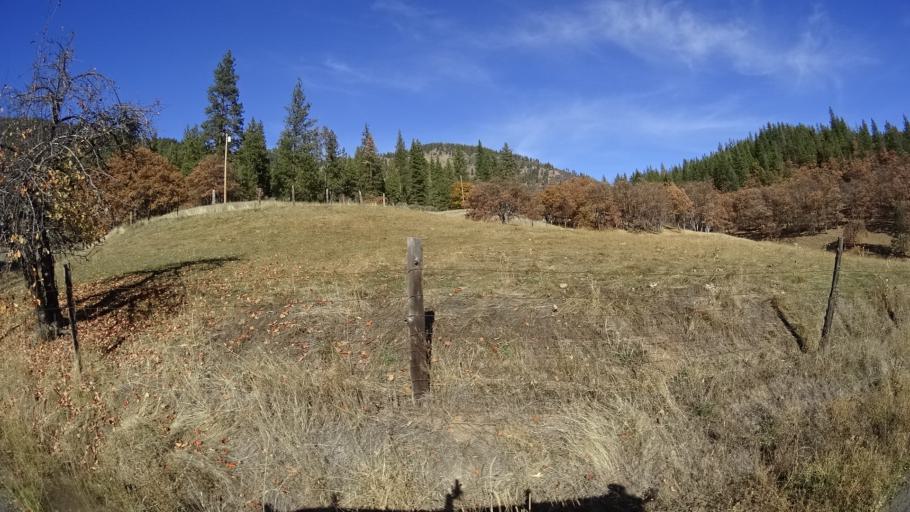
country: US
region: California
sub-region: Siskiyou County
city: Yreka
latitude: 41.7271
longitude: -122.7041
